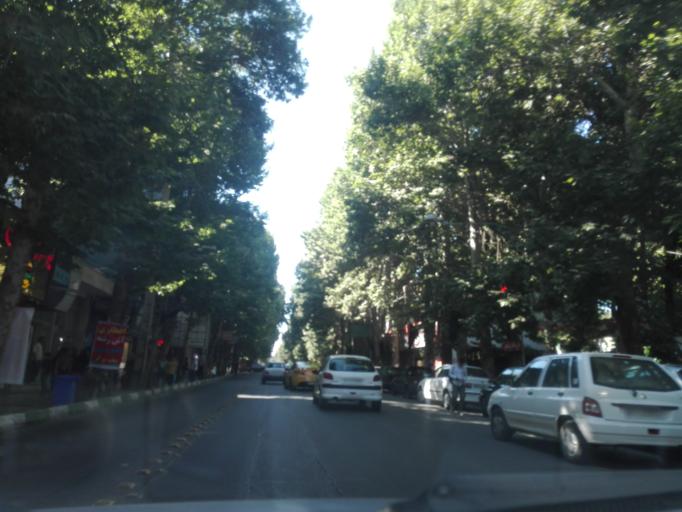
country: IR
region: Tehran
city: Shahriar
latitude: 35.6597
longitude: 51.0580
